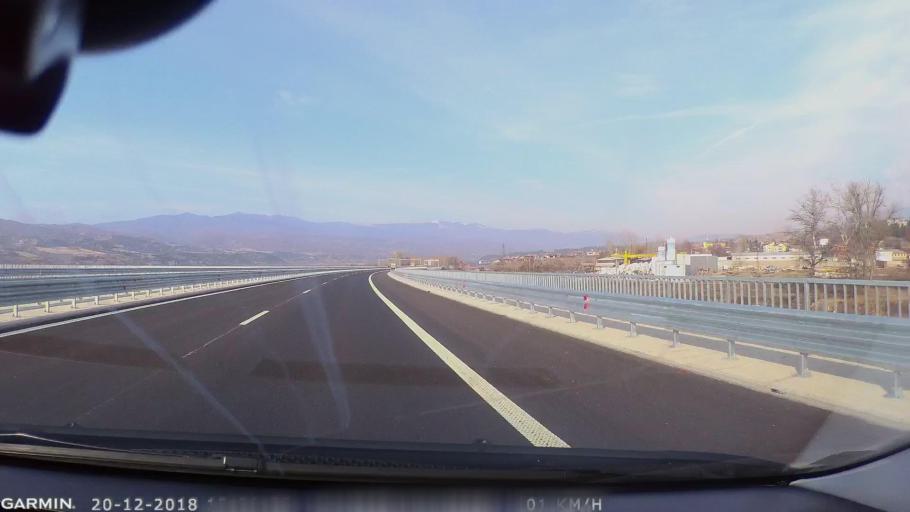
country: BG
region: Blagoevgrad
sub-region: Obshtina Strumyani
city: Strumyani
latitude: 41.6295
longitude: 23.2018
